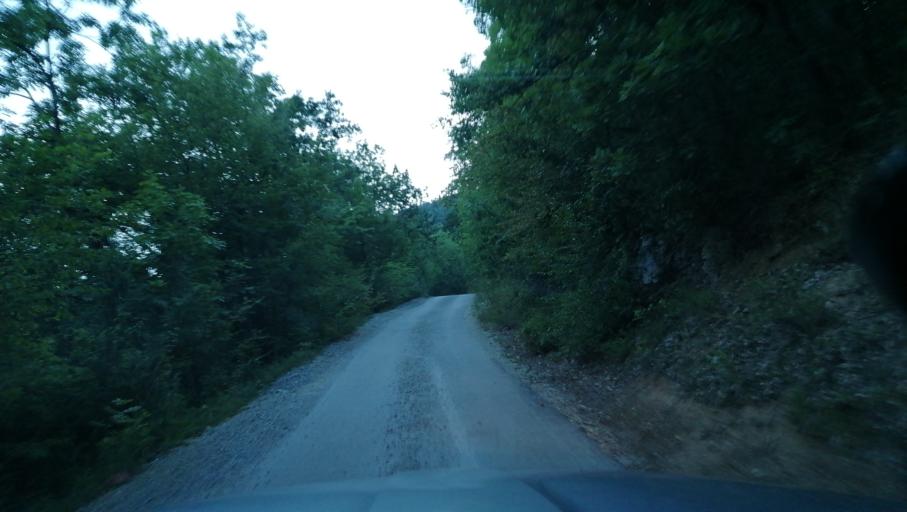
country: RS
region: Central Serbia
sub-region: Kolubarski Okrug
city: Valjevo
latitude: 44.2363
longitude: 19.8639
